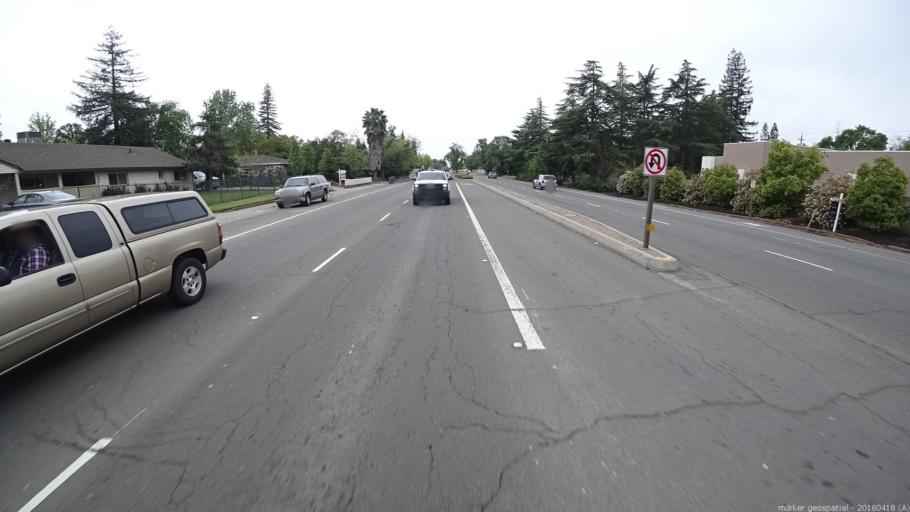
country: US
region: California
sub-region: Sacramento County
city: Arden-Arcade
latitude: 38.5784
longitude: -121.3830
